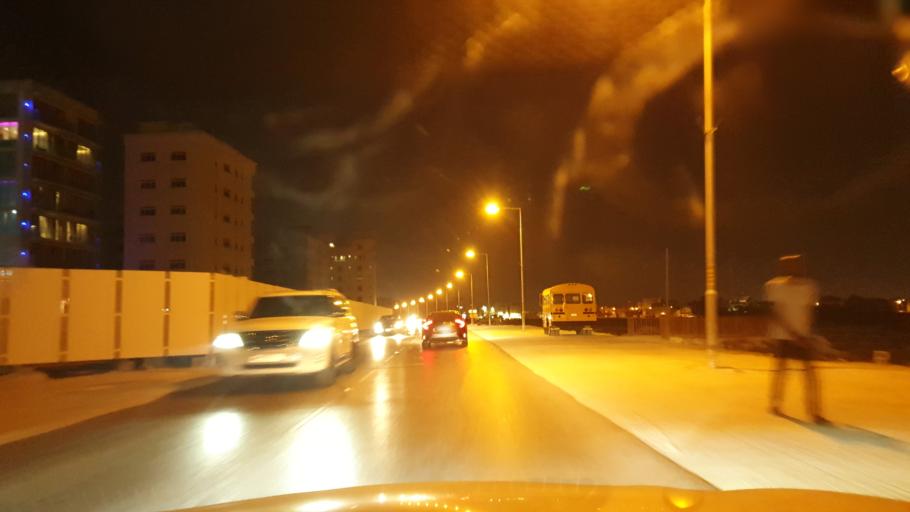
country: BH
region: Northern
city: Madinat `Isa
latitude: 26.1828
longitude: 50.4817
